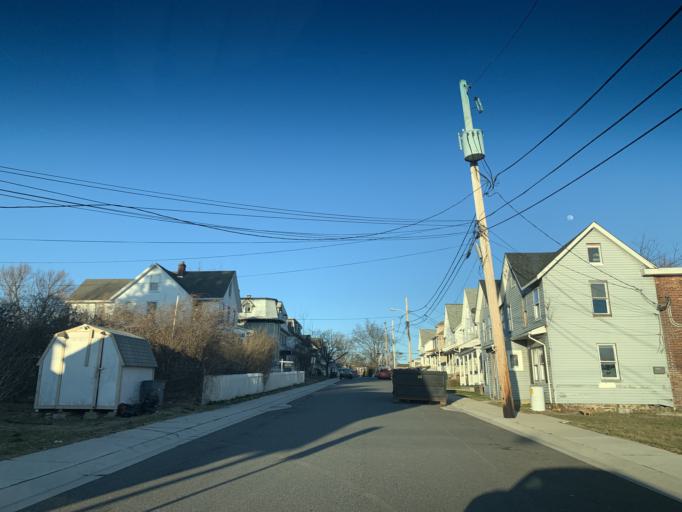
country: US
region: Maryland
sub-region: Cecil County
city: Perryville
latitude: 39.5588
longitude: -76.0769
